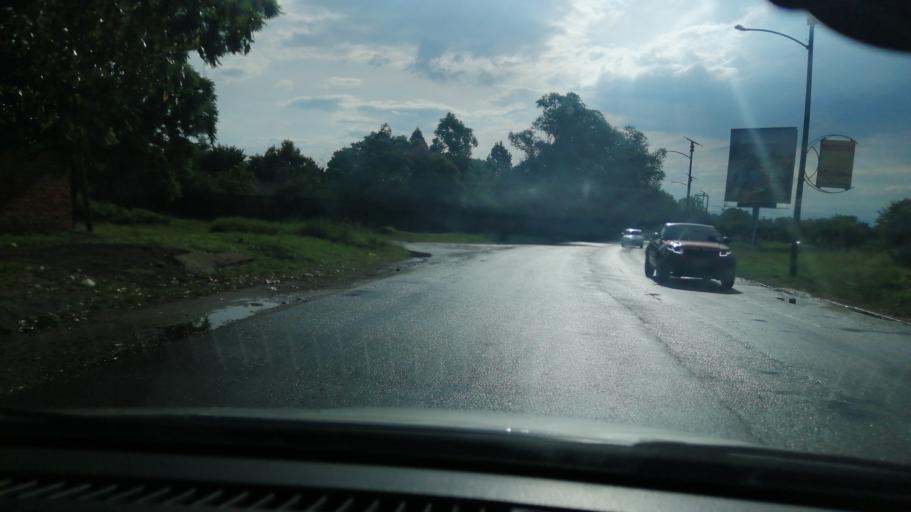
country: ZW
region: Harare
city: Harare
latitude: -17.7903
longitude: 31.0500
